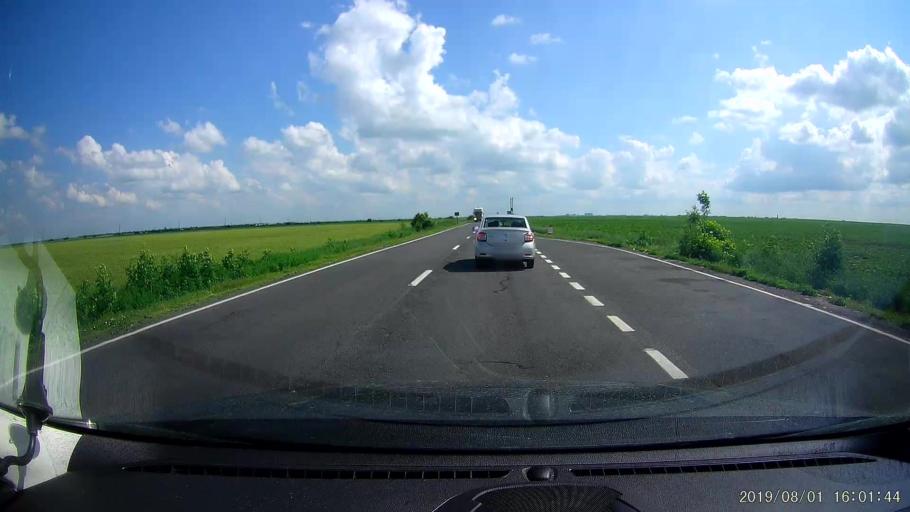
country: RO
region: Ialomita
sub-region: Comuna Ciulnita
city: Ciulnita
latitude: 44.5028
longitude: 27.3895
